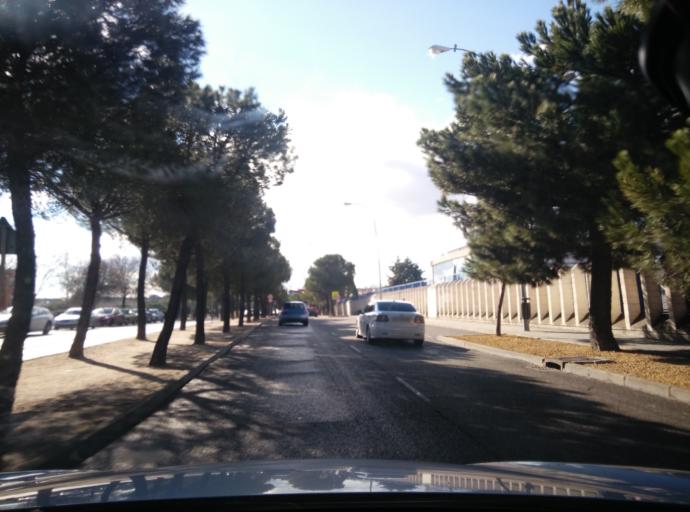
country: ES
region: Madrid
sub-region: Provincia de Madrid
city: Tres Cantos
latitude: 40.5927
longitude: -3.7060
